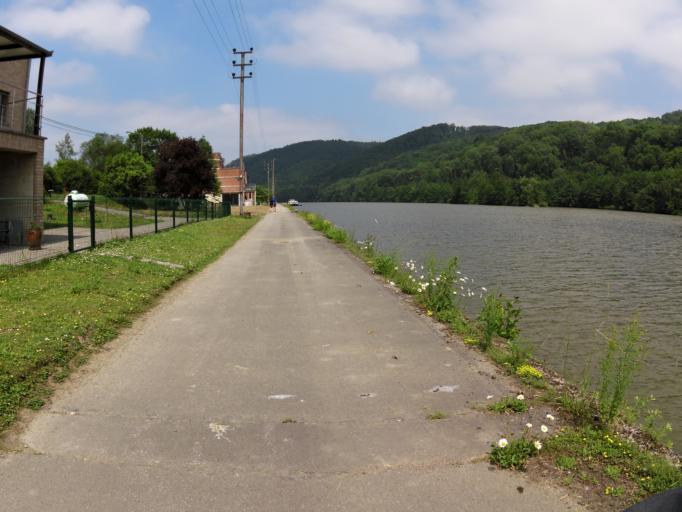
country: BE
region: Wallonia
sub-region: Province de Namur
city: Hastiere-Lavaux
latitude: 50.1868
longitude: 4.8242
